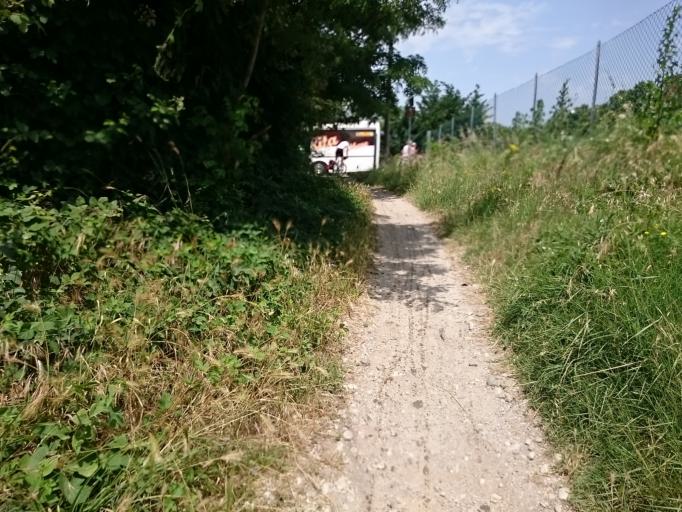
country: IT
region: Veneto
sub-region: Provincia di Venezia
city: Sant'Anna
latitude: 45.1844
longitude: 12.2782
